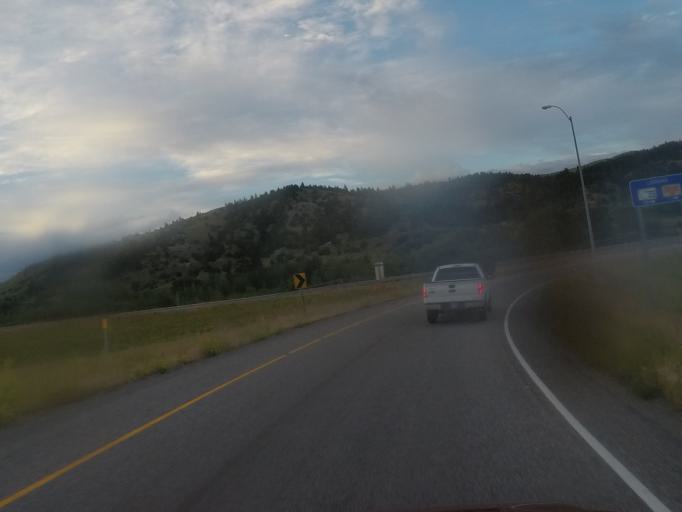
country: US
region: Montana
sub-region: Gallatin County
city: Bozeman
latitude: 45.6770
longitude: -111.0106
